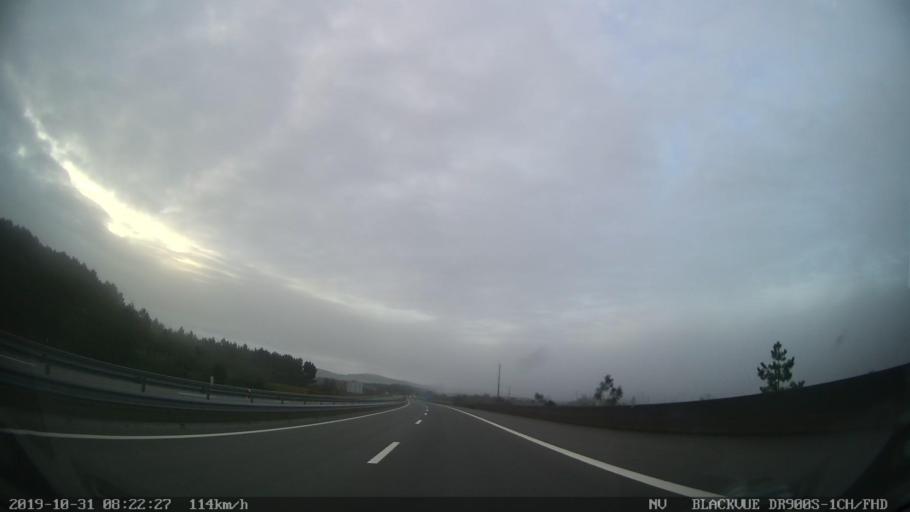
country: PT
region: Vila Real
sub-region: Vila Real
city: Vila Real
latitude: 41.2830
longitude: -7.6913
